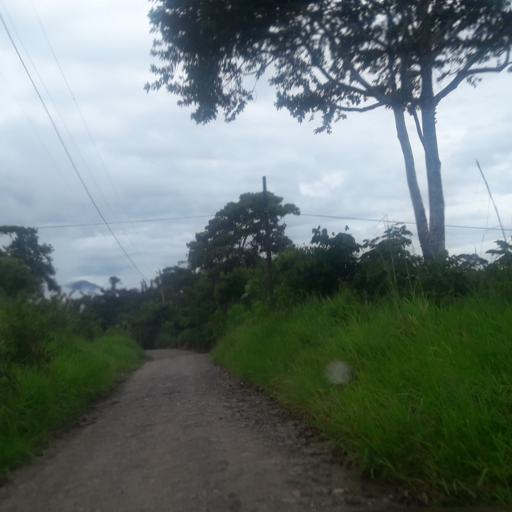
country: EC
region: Napo
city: Archidona
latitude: -0.9164
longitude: -77.8203
